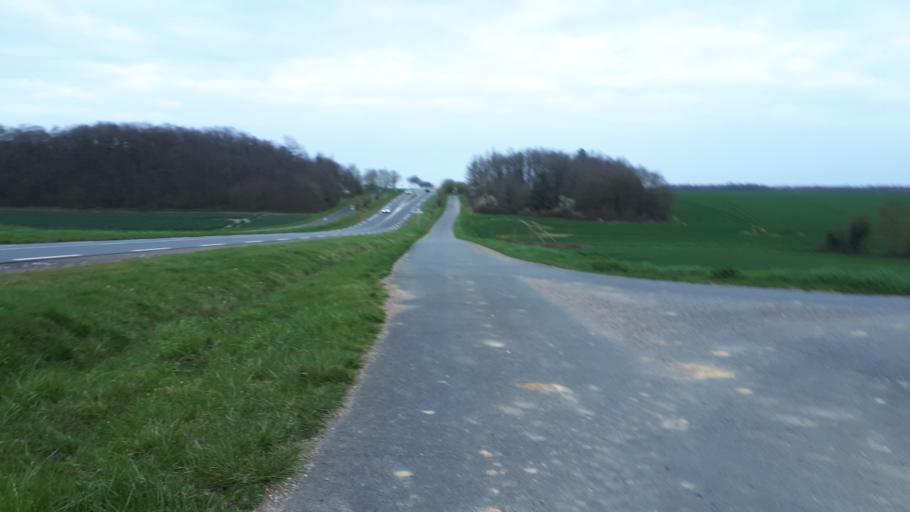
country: FR
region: Centre
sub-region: Departement du Loir-et-Cher
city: Aze
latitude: 47.8296
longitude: 1.0016
